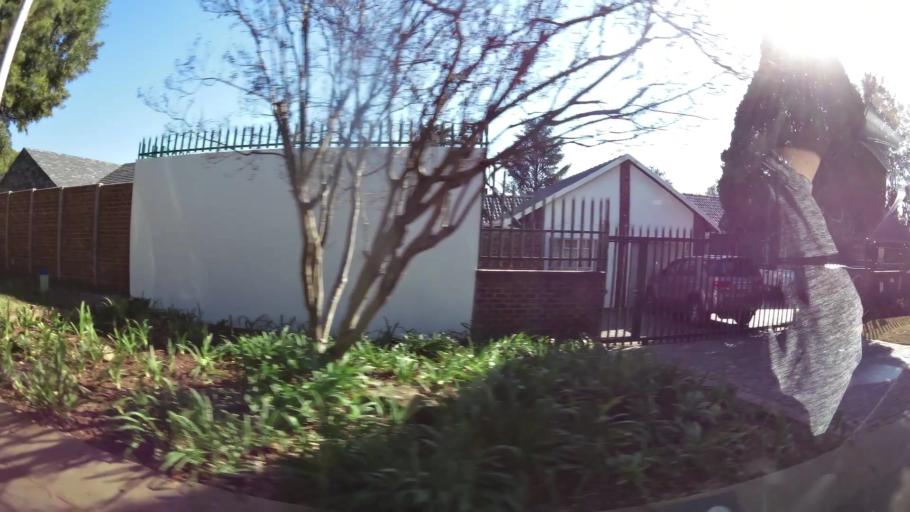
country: ZA
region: Gauteng
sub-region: City of Johannesburg Metropolitan Municipality
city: Midrand
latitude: -26.0689
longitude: 28.0473
